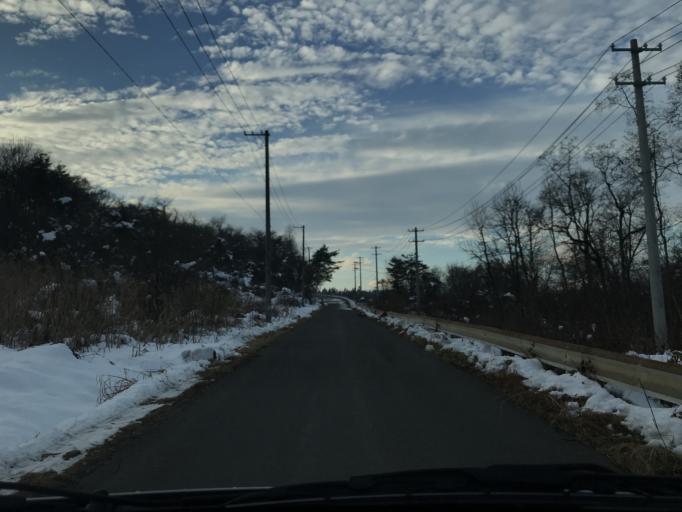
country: JP
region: Iwate
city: Mizusawa
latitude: 39.0528
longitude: 141.0733
